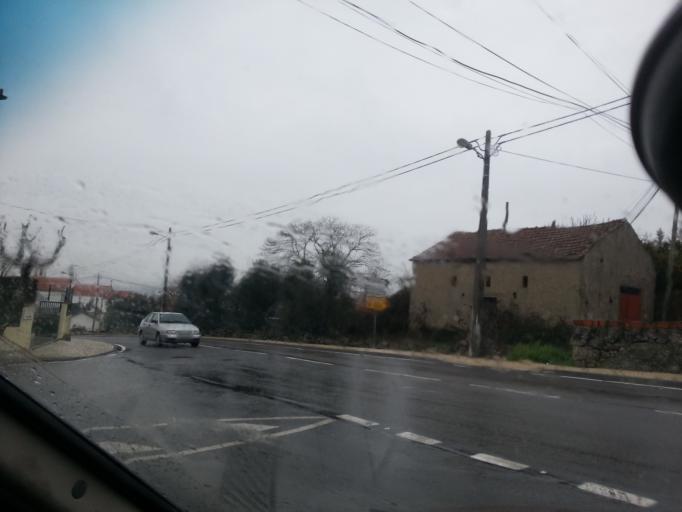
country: PT
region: Viseu
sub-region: Viseu
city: Rio de Loba
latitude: 40.6631
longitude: -7.8771
